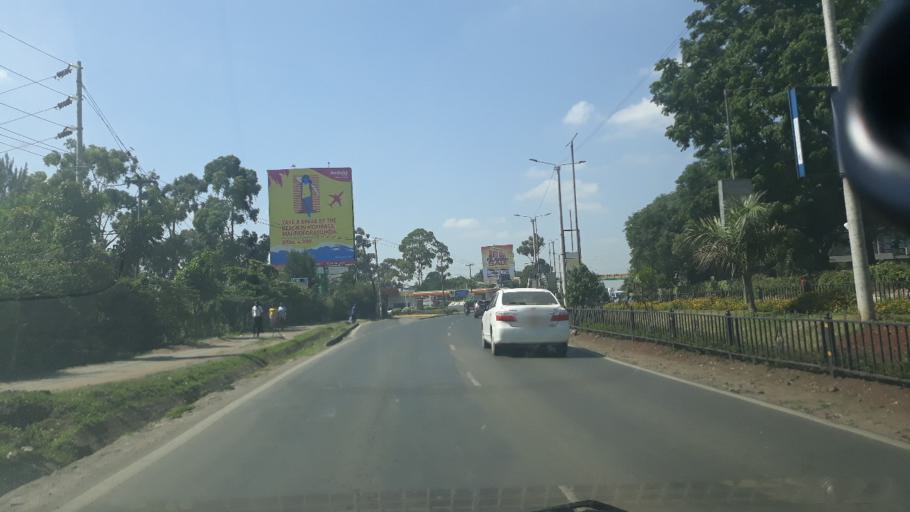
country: KE
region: Nairobi Area
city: Nairobi
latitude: -1.3150
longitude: 36.8149
